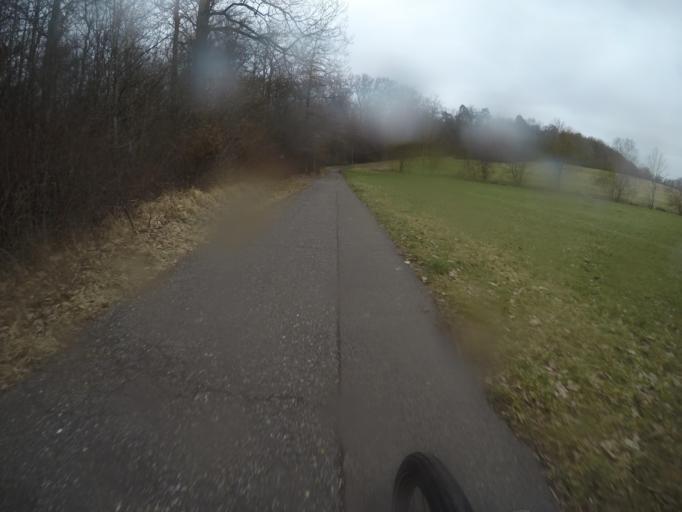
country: DE
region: Baden-Wuerttemberg
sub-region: Regierungsbezirk Stuttgart
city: Magstadt
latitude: 48.7276
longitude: 8.9944
